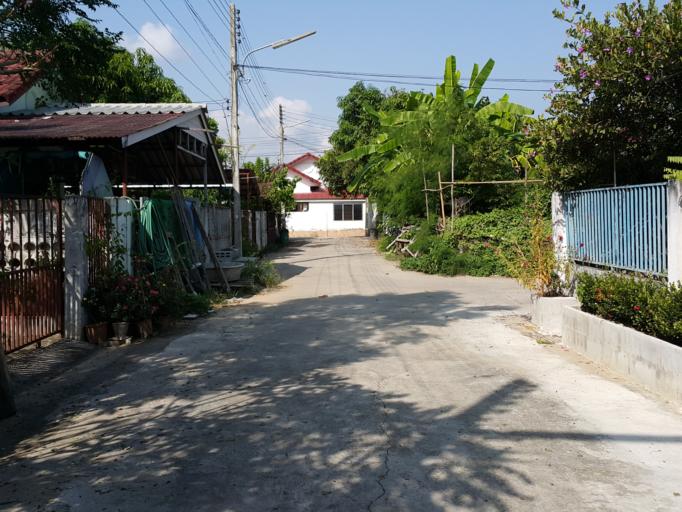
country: TH
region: Chiang Mai
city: San Kamphaeng
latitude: 18.7702
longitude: 99.0936
